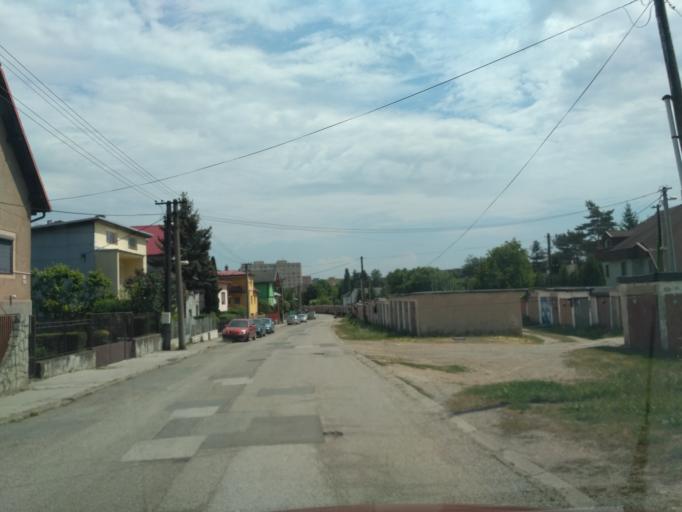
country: SK
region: Kosicky
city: Kosice
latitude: 48.7260
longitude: 21.2341
